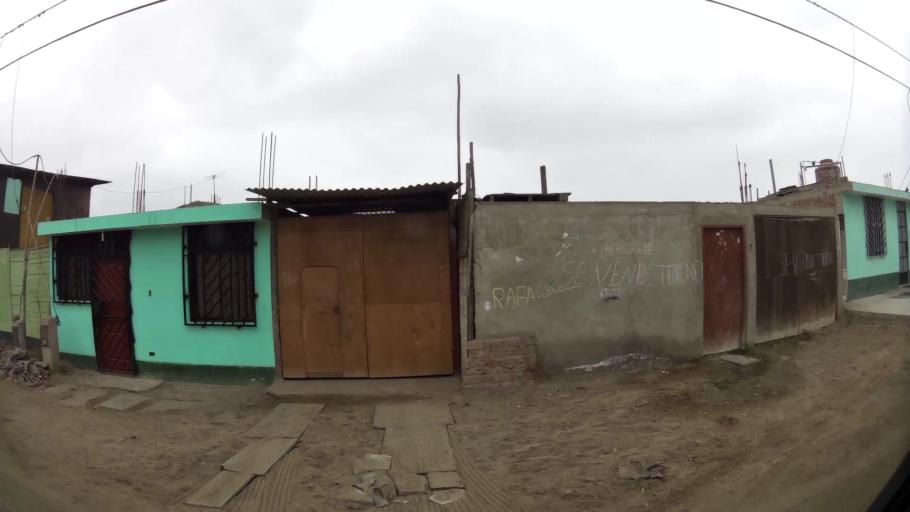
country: PE
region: Lima
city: Ventanilla
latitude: -11.8493
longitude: -77.1334
